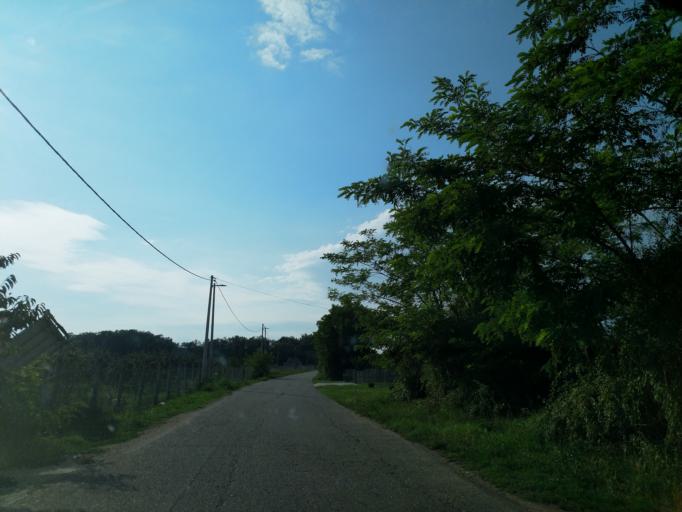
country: RS
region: Central Serbia
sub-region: Pomoravski Okrug
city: Jagodina
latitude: 43.9861
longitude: 21.2151
